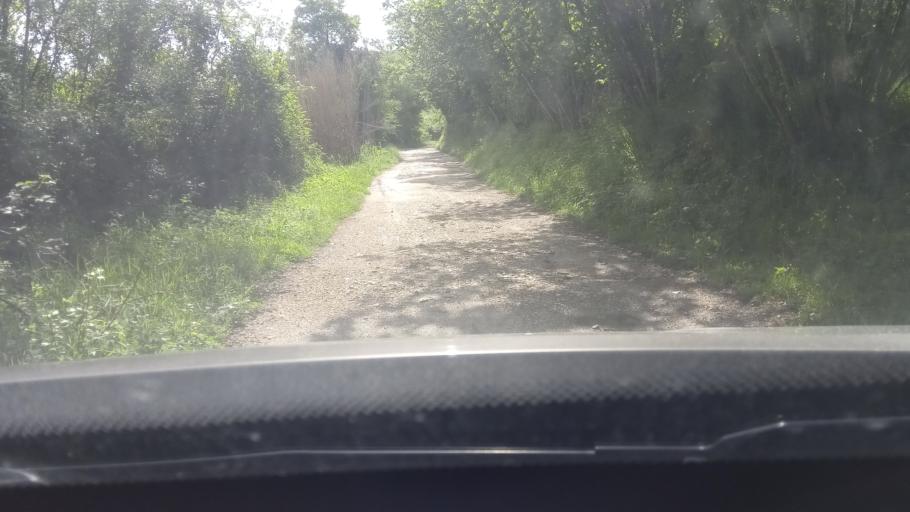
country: IT
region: Latium
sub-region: Provincia di Latina
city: Minturno
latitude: 41.2808
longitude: 13.7635
